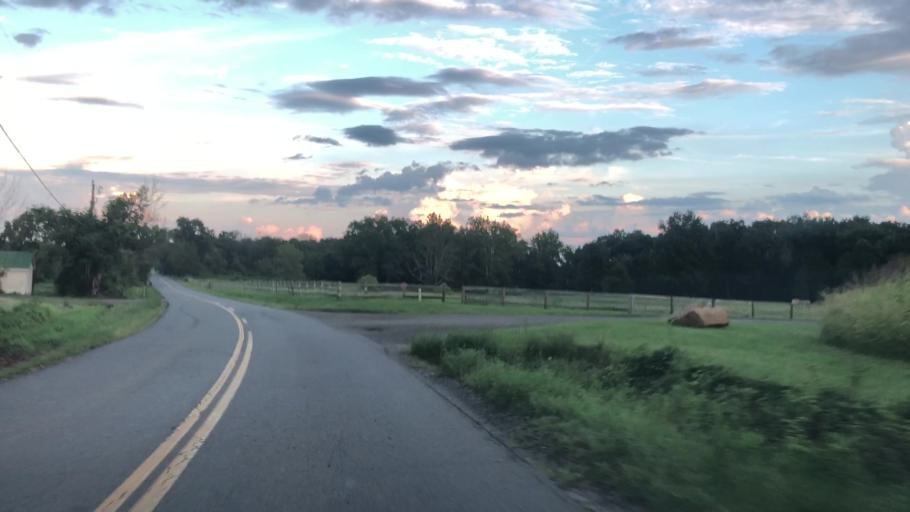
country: US
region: Virginia
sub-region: Prince William County
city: Nokesville
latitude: 38.6782
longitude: -77.6655
